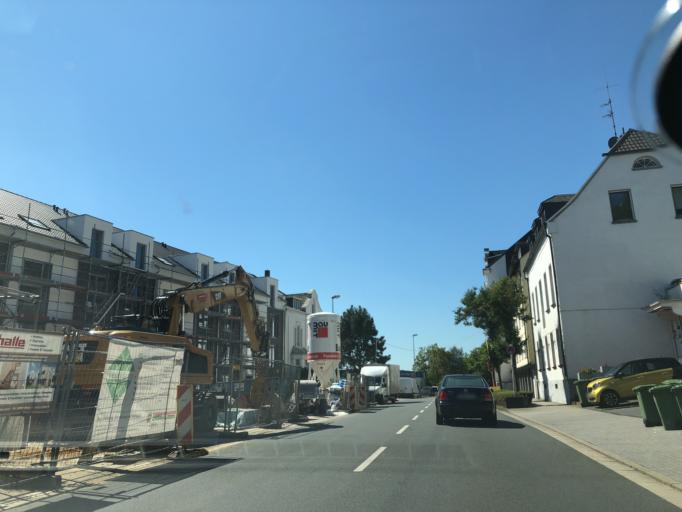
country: DE
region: North Rhine-Westphalia
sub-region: Regierungsbezirk Dusseldorf
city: Muelheim (Ruhr)
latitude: 51.4220
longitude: 6.8725
